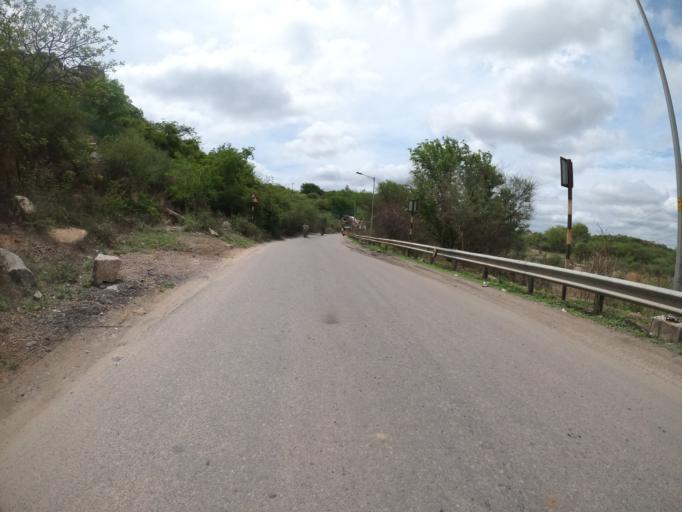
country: IN
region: Telangana
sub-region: Hyderabad
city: Hyderabad
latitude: 17.3169
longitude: 78.3716
